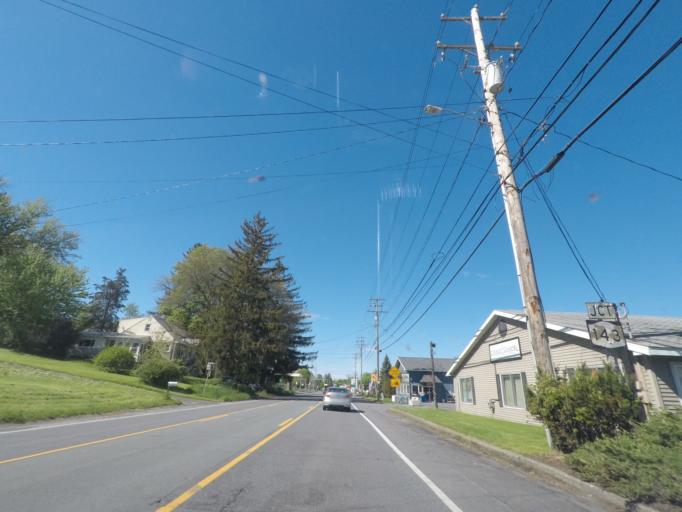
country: US
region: New York
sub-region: Albany County
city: Ravena
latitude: 42.4663
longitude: -73.8164
